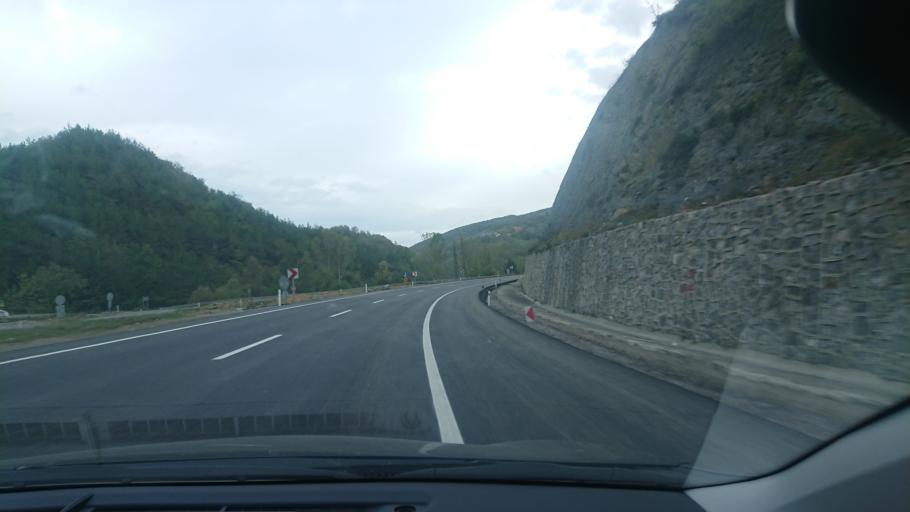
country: TR
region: Zonguldak
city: Beycuma
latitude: 41.3962
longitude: 31.9361
